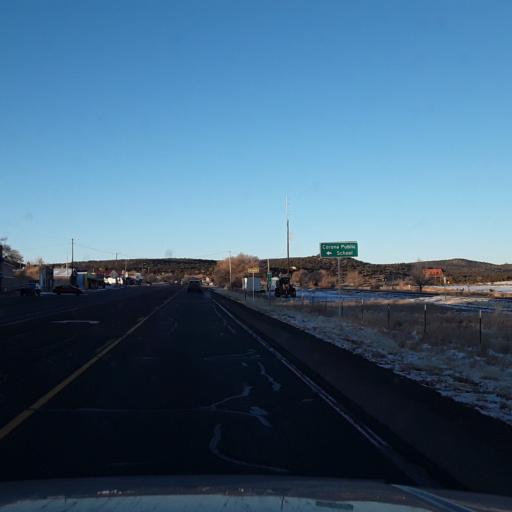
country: US
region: New Mexico
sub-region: Lincoln County
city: Carrizozo
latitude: 34.2484
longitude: -105.5948
